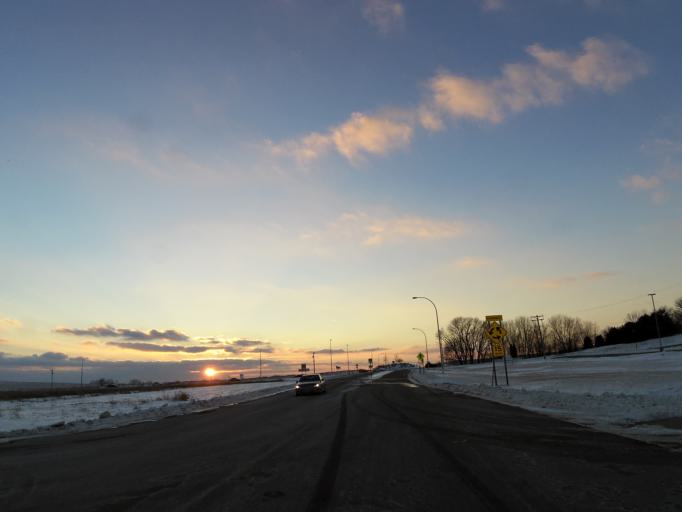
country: US
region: Minnesota
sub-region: Dakota County
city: Farmington
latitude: 44.6737
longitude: -93.1342
